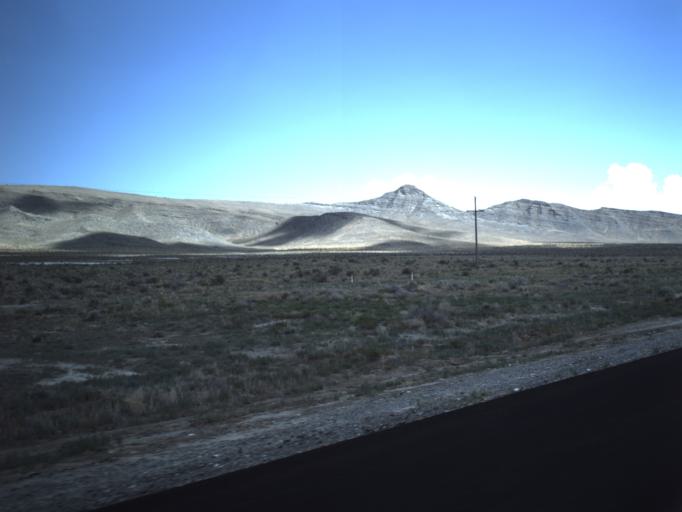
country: US
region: Utah
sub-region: Beaver County
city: Milford
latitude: 39.0484
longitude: -113.4154
